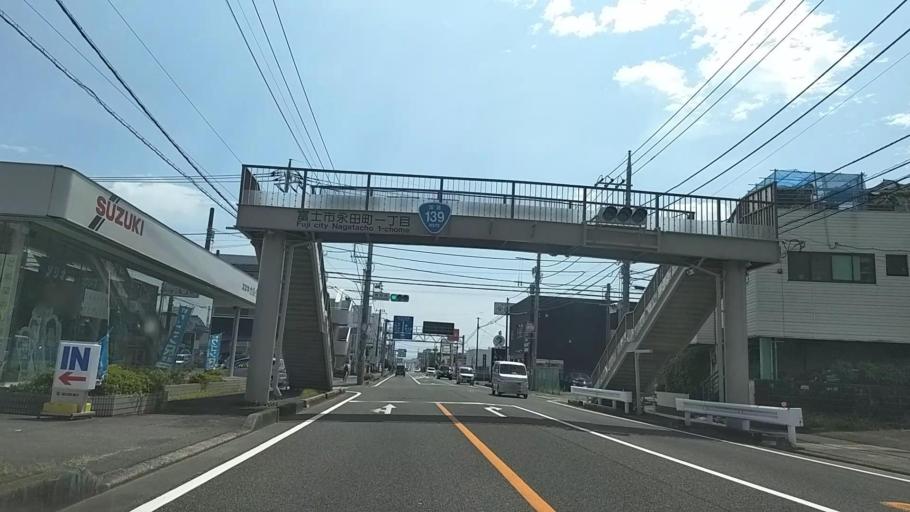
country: JP
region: Shizuoka
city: Fuji
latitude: 35.1594
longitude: 138.6781
